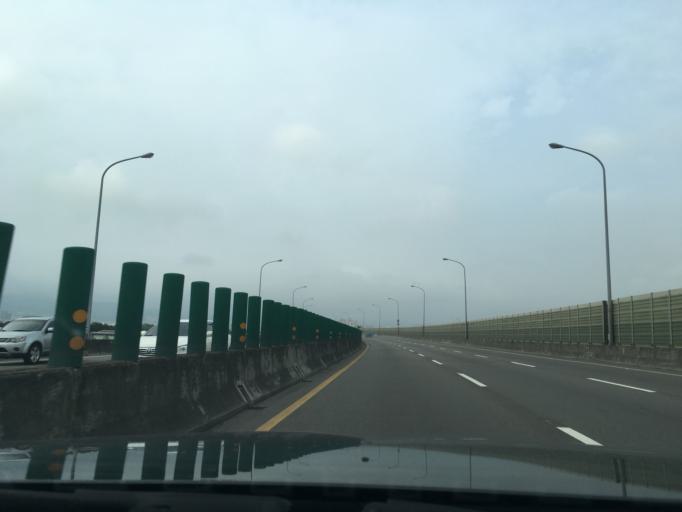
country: TW
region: Taipei
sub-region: Taipei
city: Banqiao
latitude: 25.0119
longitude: 121.4508
